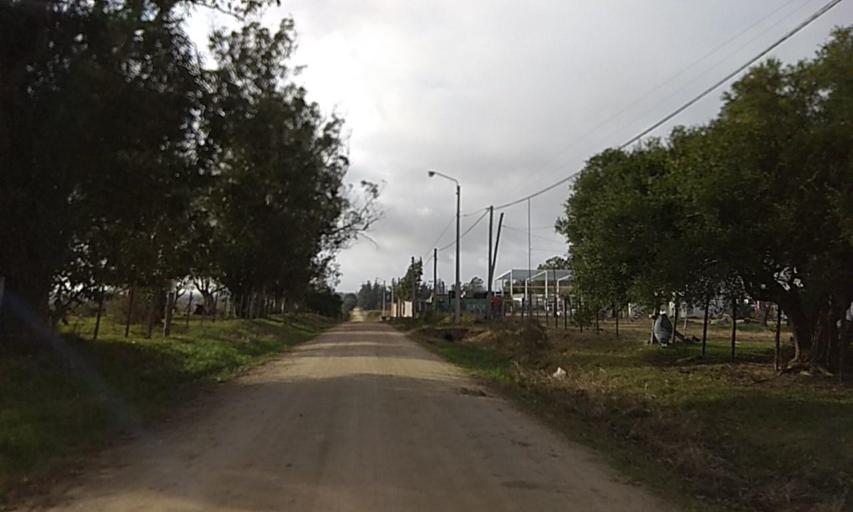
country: UY
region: Florida
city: Florida
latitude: -34.0777
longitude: -56.2210
